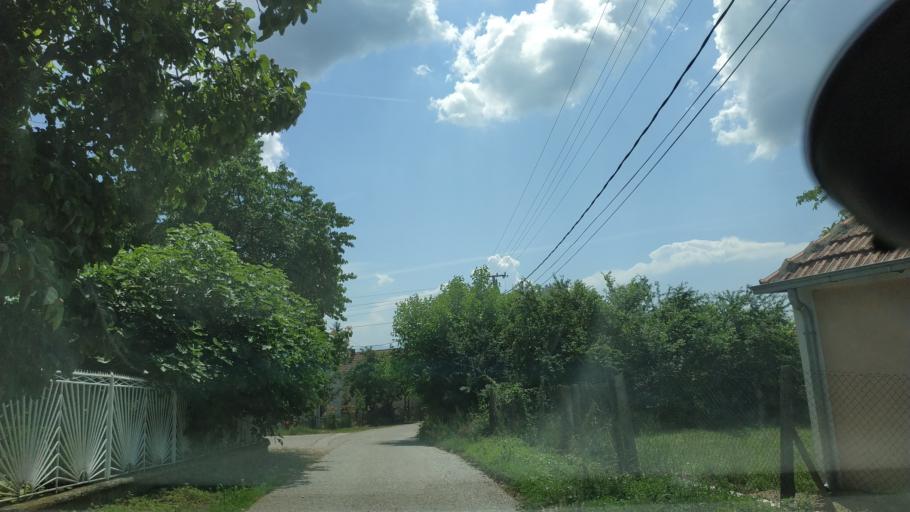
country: RS
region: Central Serbia
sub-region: Nisavski Okrug
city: Aleksinac
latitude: 43.6011
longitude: 21.6957
